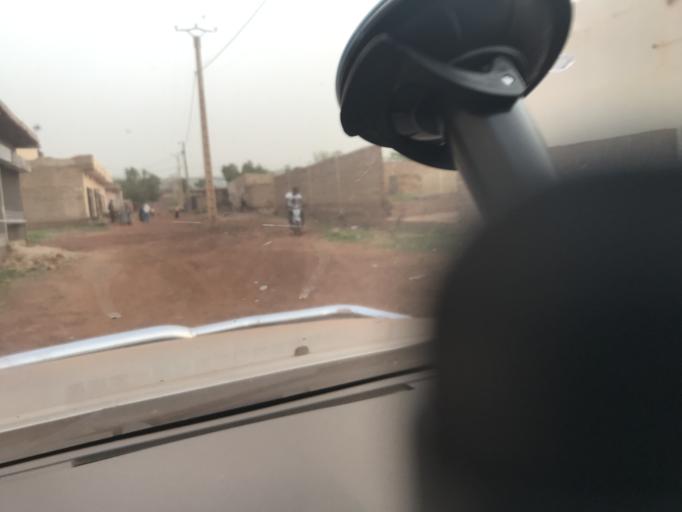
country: ML
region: Bamako
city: Bamako
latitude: 12.6536
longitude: -7.8910
